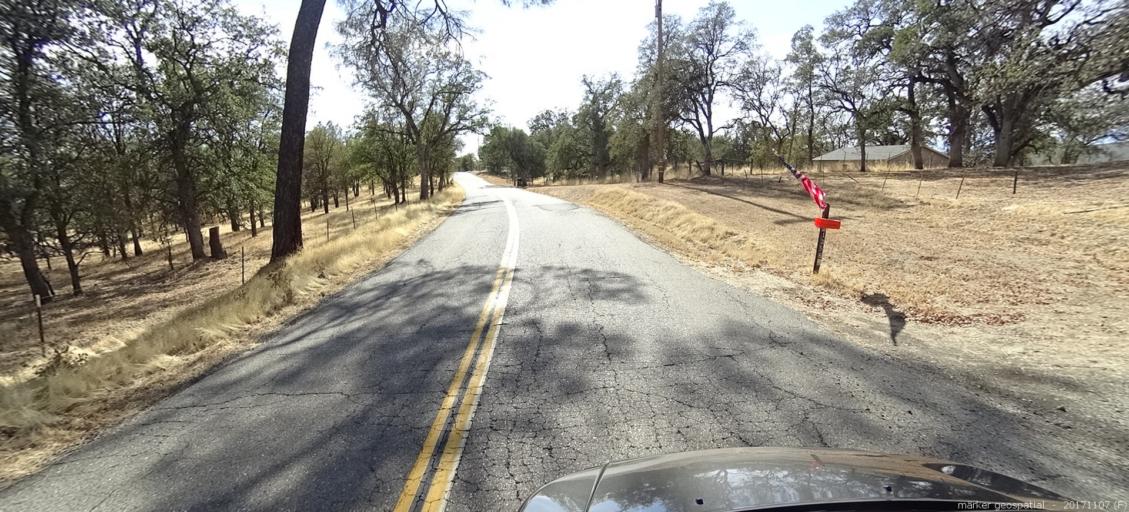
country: US
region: California
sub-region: Shasta County
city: Shasta
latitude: 40.4296
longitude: -122.5211
